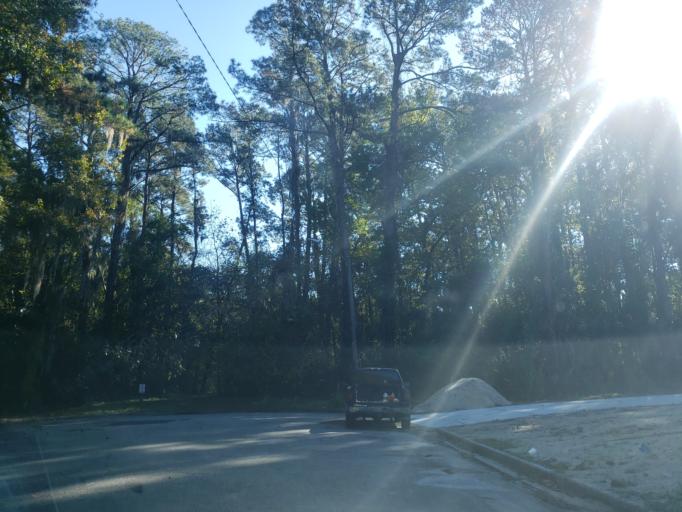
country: US
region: Georgia
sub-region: Chatham County
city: Isle of Hope
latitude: 31.9975
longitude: -81.1017
